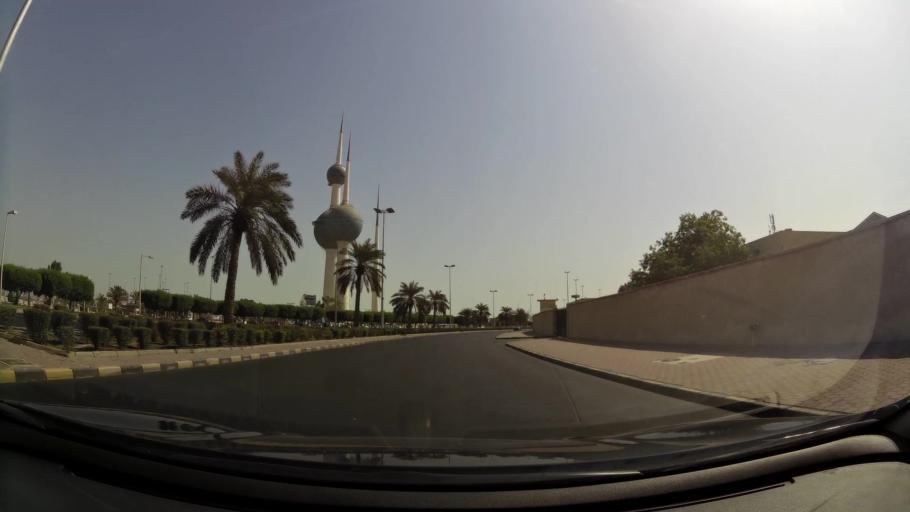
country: KW
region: Al Asimah
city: Ad Dasmah
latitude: 29.3903
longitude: 47.9999
